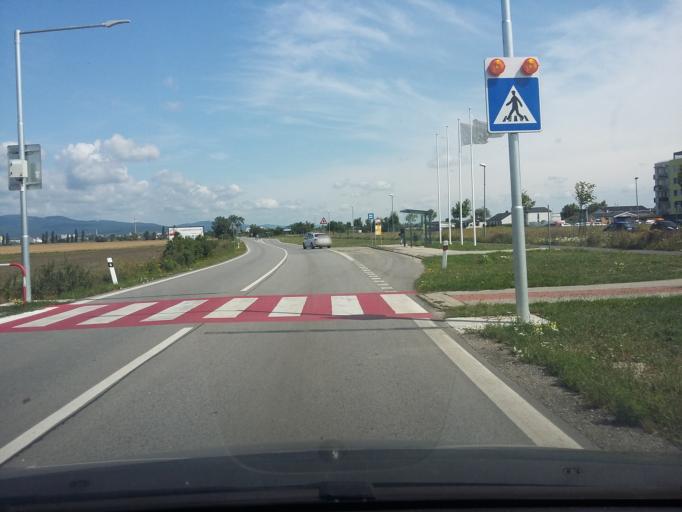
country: SK
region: Bratislavsky
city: Svaty Jur
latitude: 48.2438
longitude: 17.2591
